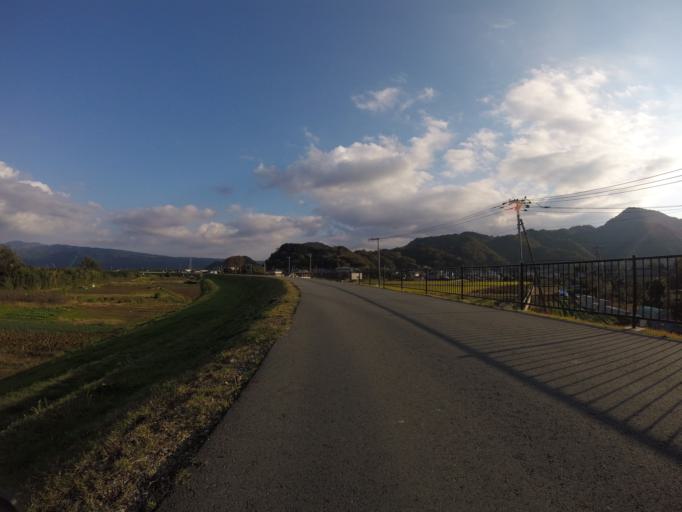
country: JP
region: Shizuoka
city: Mishima
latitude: 35.0761
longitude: 138.9134
